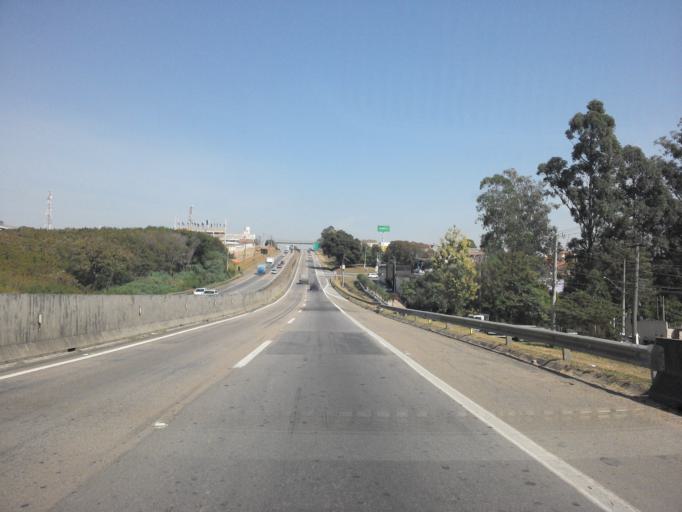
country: BR
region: Sao Paulo
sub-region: Hortolandia
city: Hortolandia
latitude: -22.8976
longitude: -47.1918
